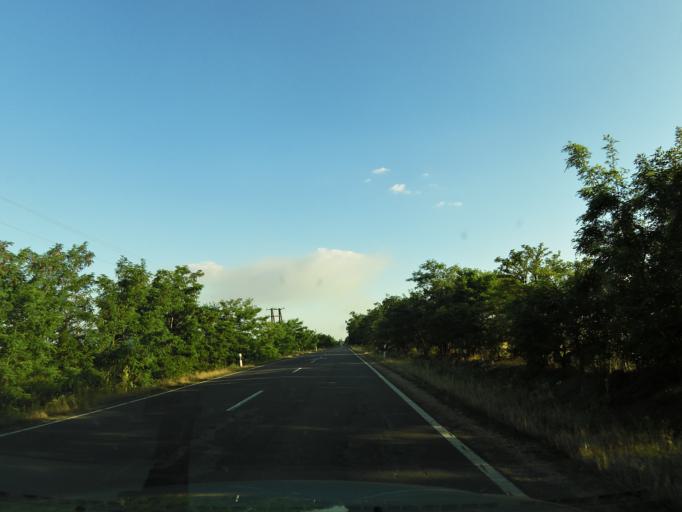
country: HU
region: Jasz-Nagykun-Szolnok
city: Kunszentmarton
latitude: 46.8562
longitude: 20.2657
